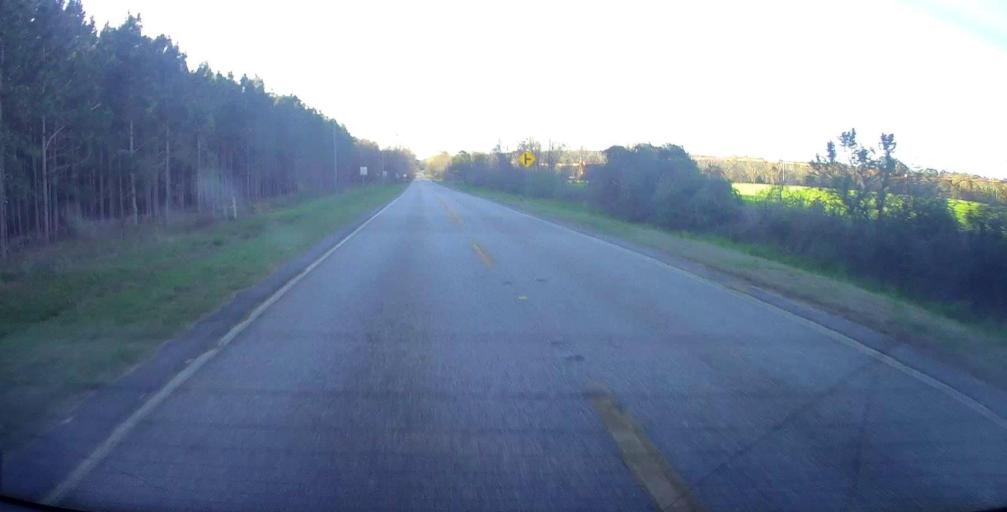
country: US
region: Georgia
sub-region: Wilcox County
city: Abbeville
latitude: 32.1156
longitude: -83.3226
